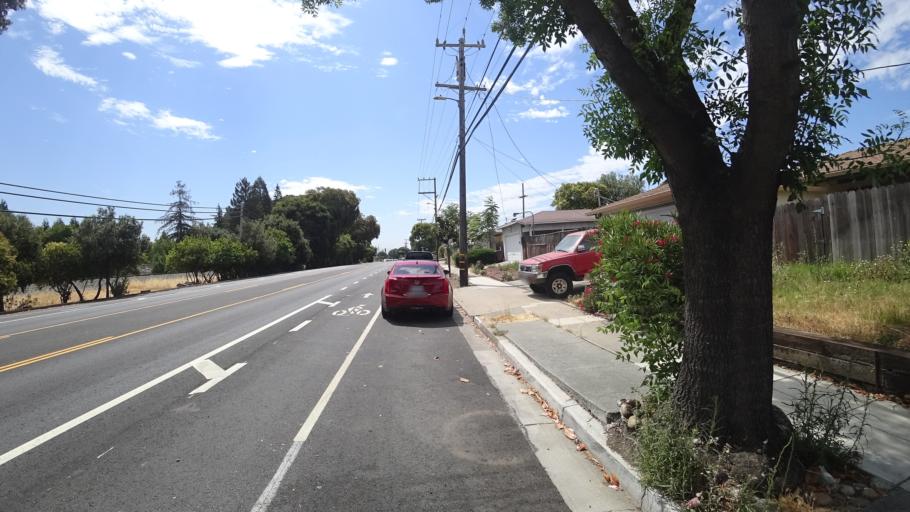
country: US
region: California
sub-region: Alameda County
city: Hayward
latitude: 37.6435
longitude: -122.0743
